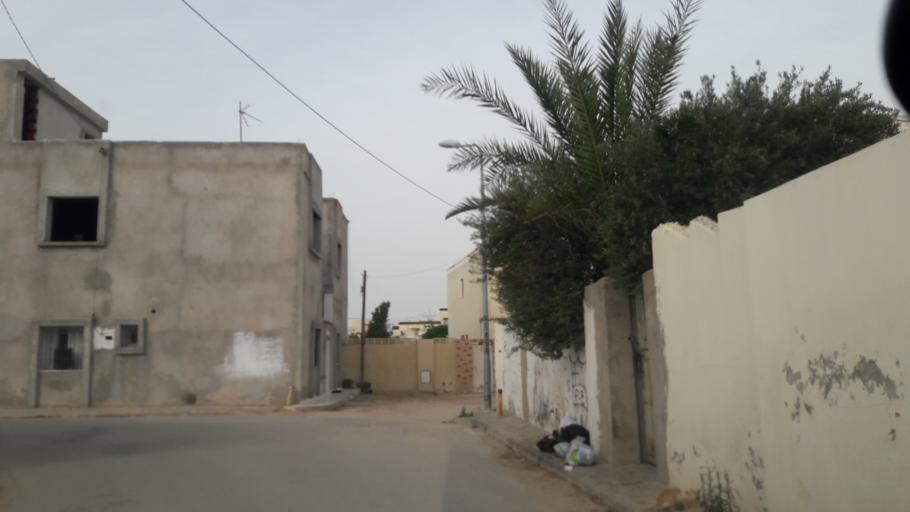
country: TN
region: Safaqis
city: Al Qarmadah
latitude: 34.7766
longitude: 10.7643
